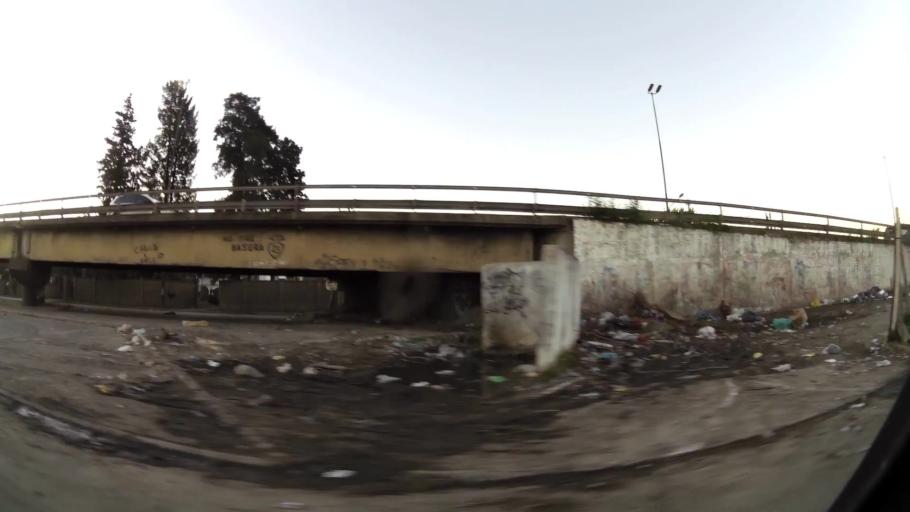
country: AR
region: Buenos Aires
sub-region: Partido de Almirante Brown
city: Adrogue
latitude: -34.8012
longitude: -58.3290
